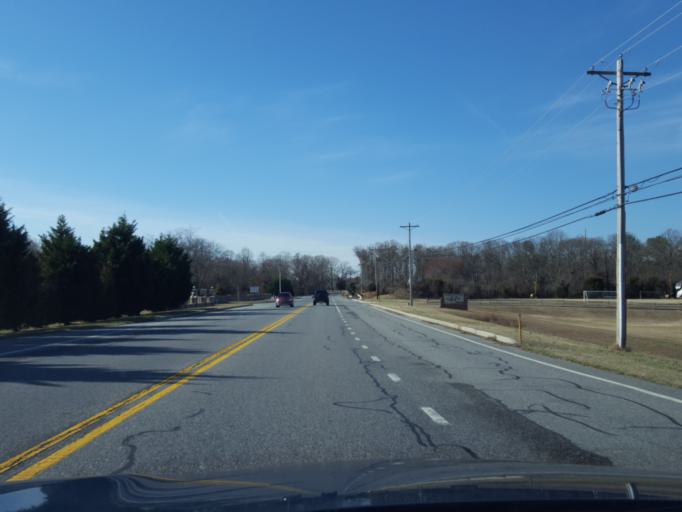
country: US
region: Maryland
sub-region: Calvert County
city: Prince Frederick
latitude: 38.4907
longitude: -76.5370
